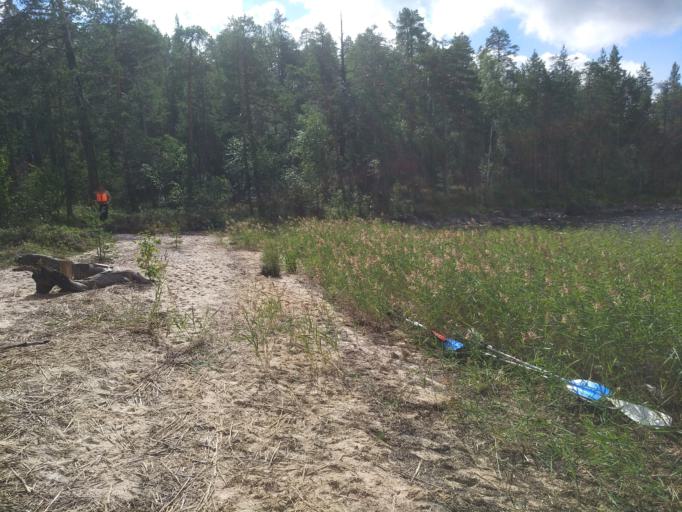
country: RU
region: Republic of Karelia
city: Kalevala
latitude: 64.8131
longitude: 31.0499
